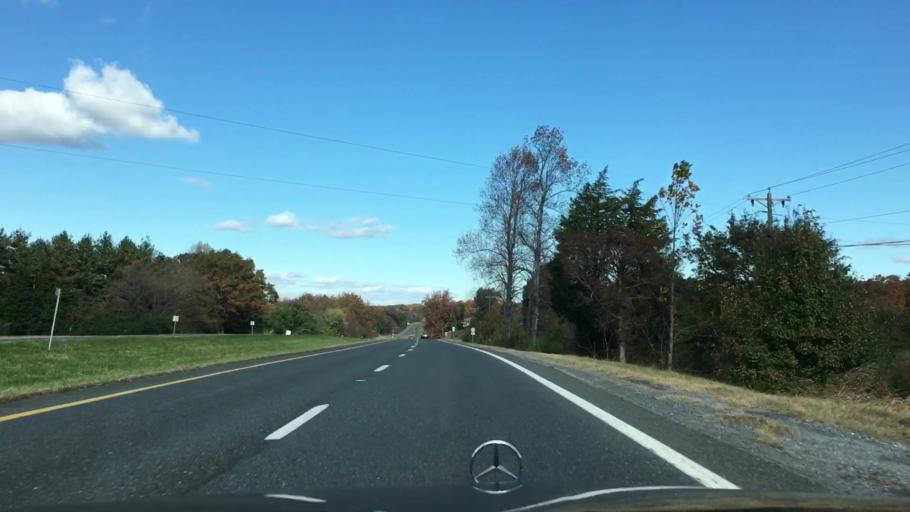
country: US
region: Virginia
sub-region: Campbell County
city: Altavista
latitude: 37.1864
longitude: -79.2037
